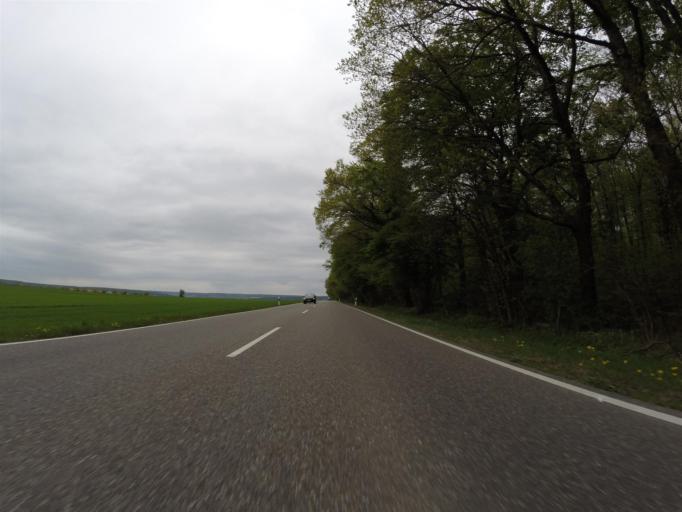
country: DE
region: Saxony-Anhalt
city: Naumburg
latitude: 51.1276
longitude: 11.7877
